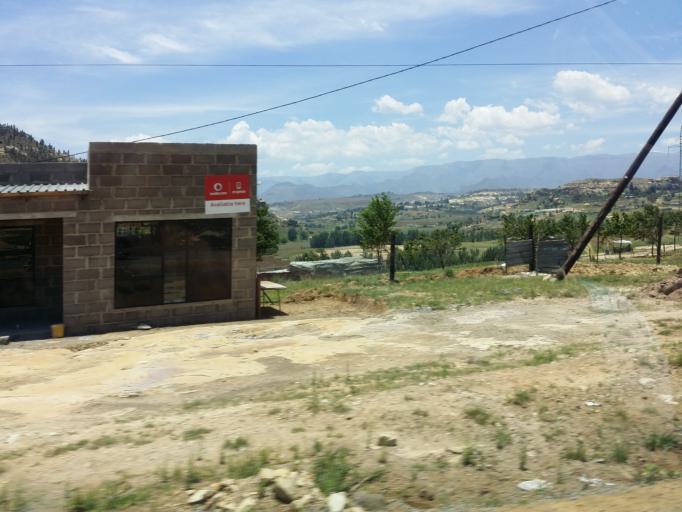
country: LS
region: Butha-Buthe
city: Butha-Buthe
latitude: -28.7228
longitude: 28.3865
